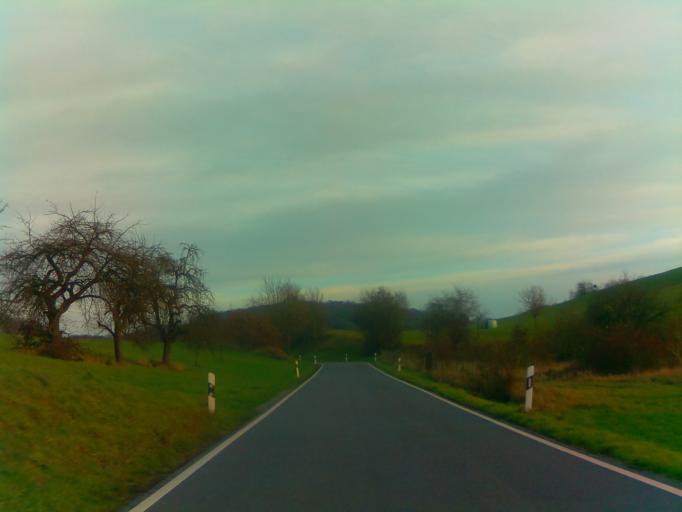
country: DE
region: Hesse
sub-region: Regierungsbezirk Darmstadt
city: Morlenbach
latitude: 49.5809
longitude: 8.7252
